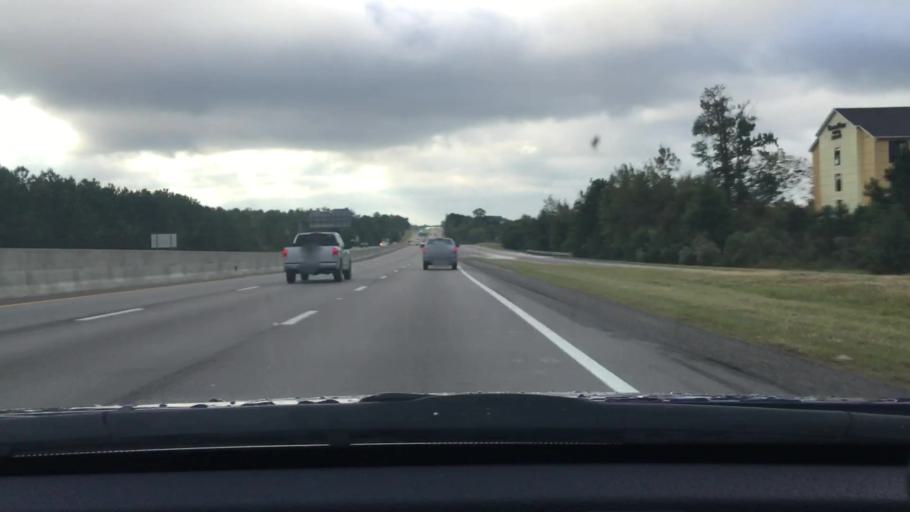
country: US
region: South Carolina
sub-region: Lexington County
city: Irmo
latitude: 34.0892
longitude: -81.1639
